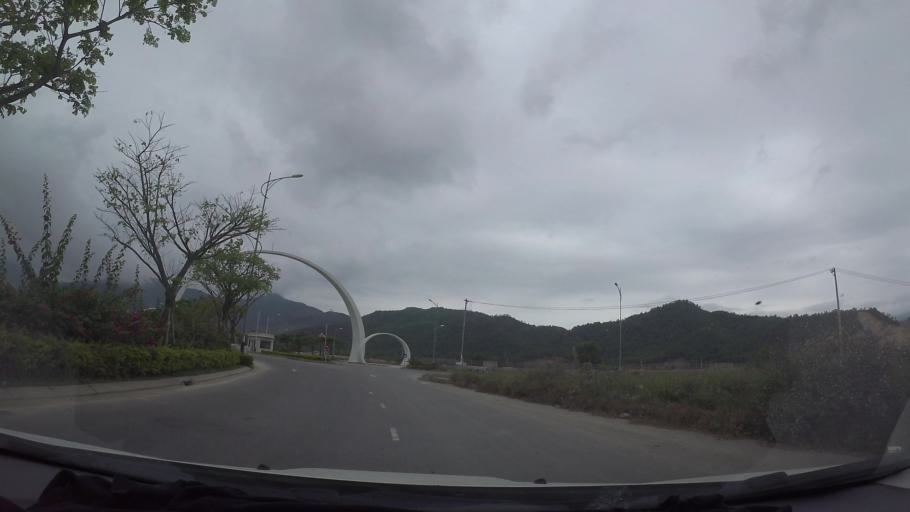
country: VN
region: Da Nang
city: Lien Chieu
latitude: 16.0933
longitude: 108.0864
